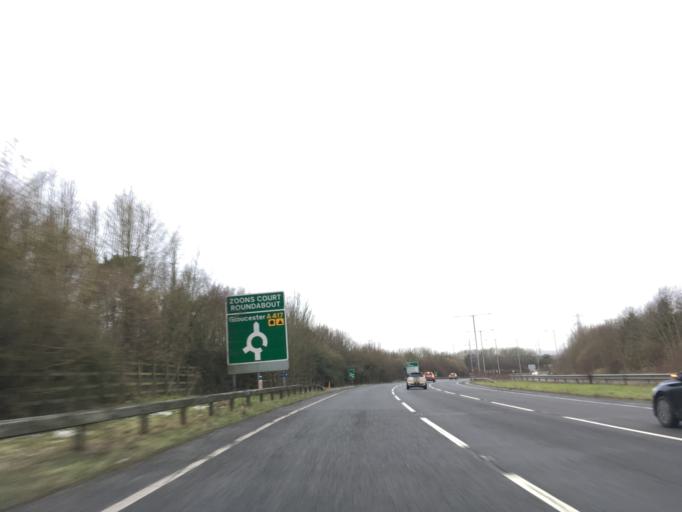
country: GB
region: England
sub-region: Gloucestershire
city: Barnwood
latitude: 51.8593
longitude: -2.1810
